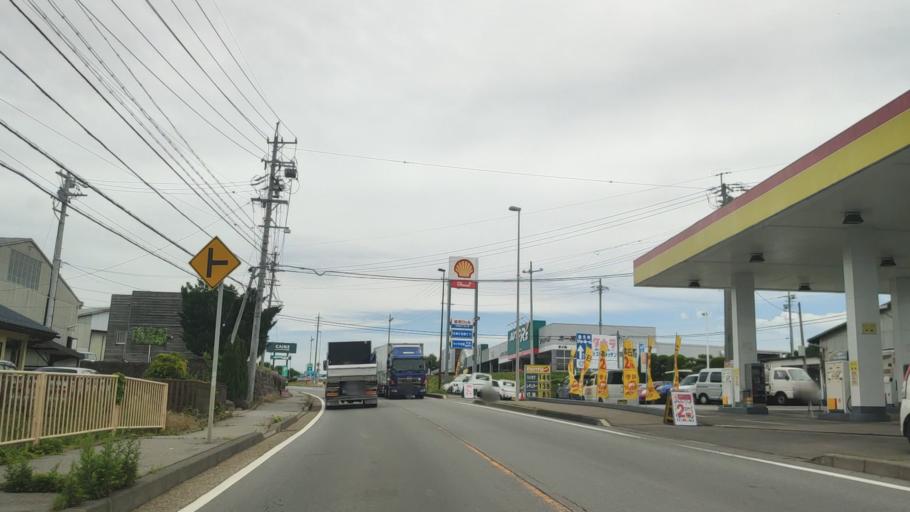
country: JP
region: Nagano
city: Komoro
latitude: 36.3408
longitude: 138.3900
